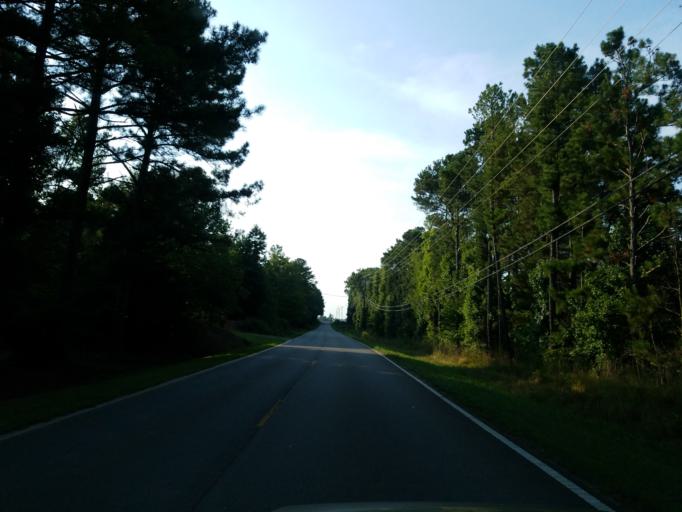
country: US
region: Georgia
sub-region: Pickens County
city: Jasper
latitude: 34.5331
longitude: -84.5306
